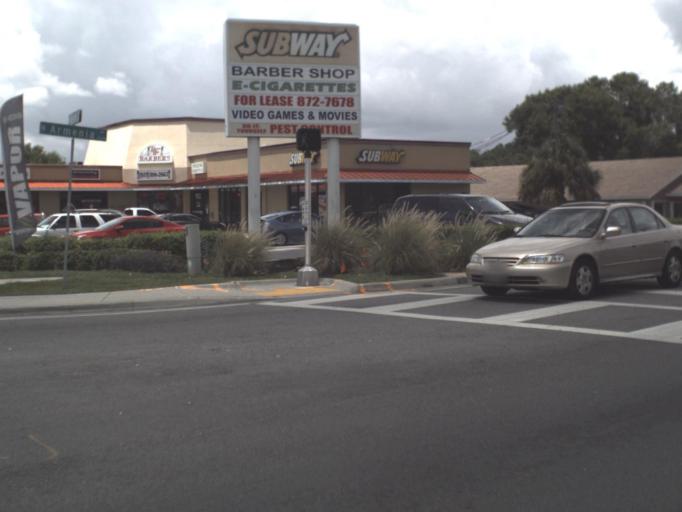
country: US
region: Florida
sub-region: Hillsborough County
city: Carrollwood
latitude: 28.0335
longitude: -82.4841
